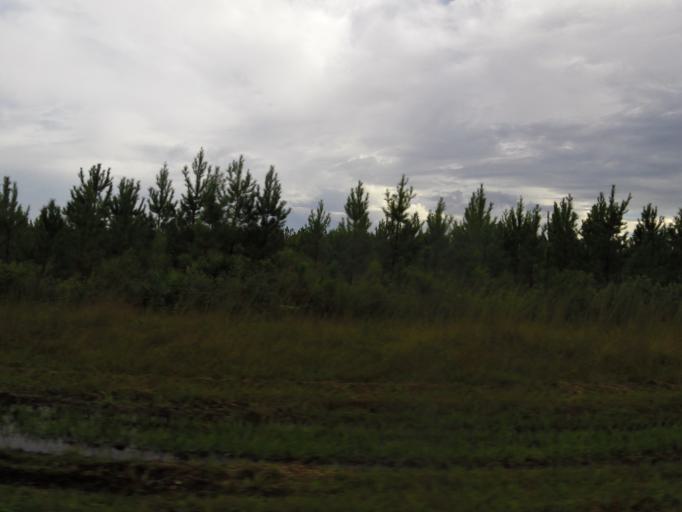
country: US
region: Florida
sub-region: Duval County
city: Baldwin
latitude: 30.4020
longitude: -81.9745
